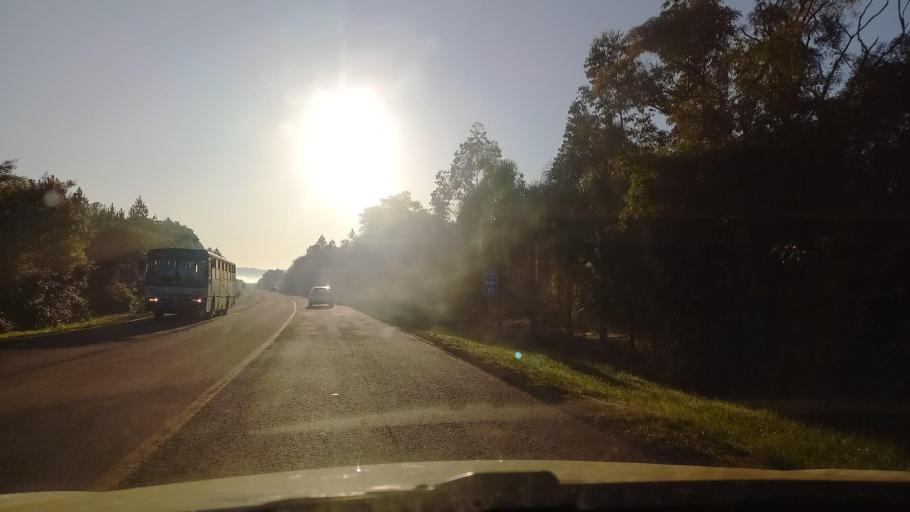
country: BR
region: Rio Grande do Sul
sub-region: Santa Cruz Do Sul
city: Santa Cruz do Sul
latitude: -29.7000
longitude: -52.5132
